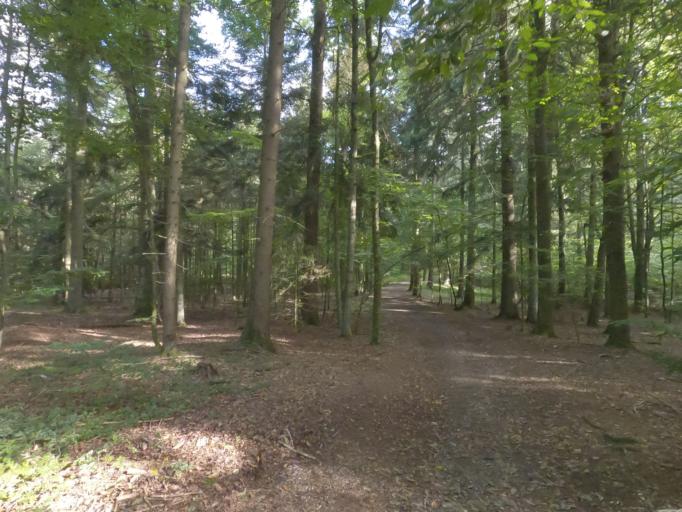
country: DE
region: Bavaria
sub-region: Lower Bavaria
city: Niederalteich
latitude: 48.8036
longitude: 13.0231
